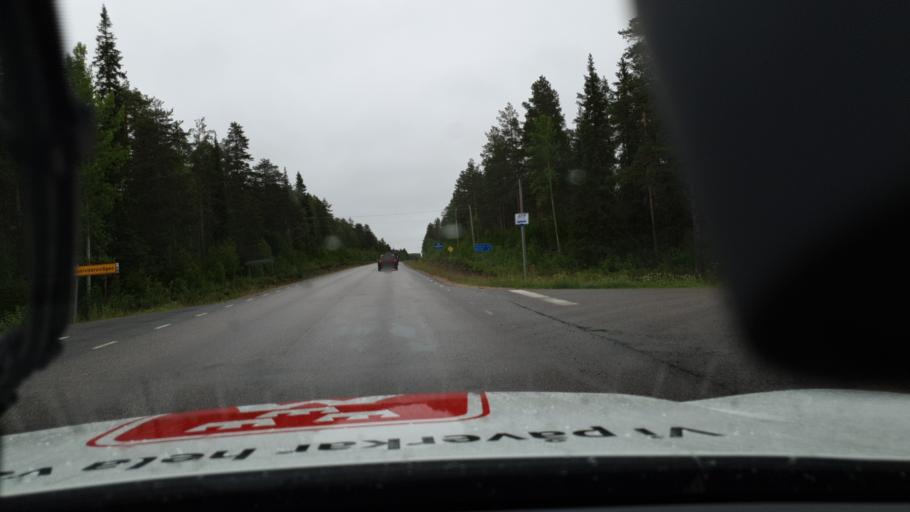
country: SE
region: Norrbotten
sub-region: Overtornea Kommun
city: OEvertornea
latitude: 66.5125
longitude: 23.7344
